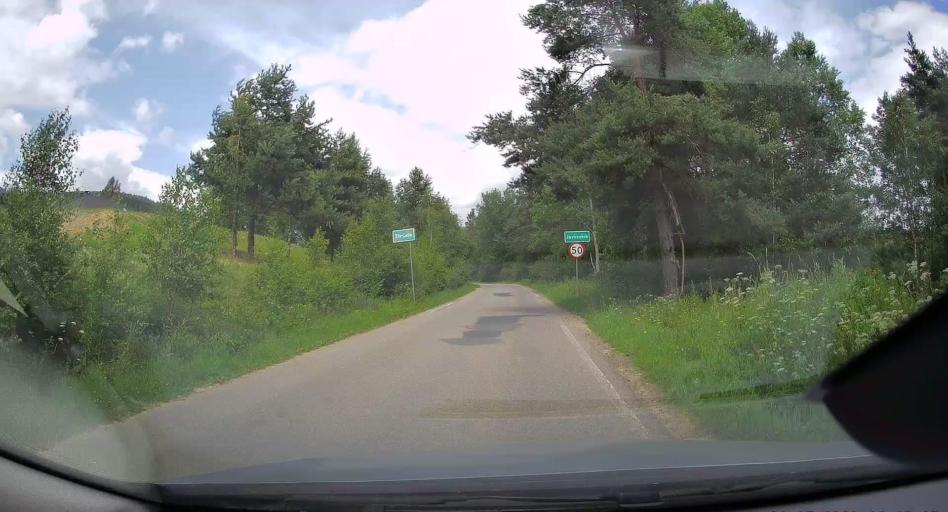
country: PL
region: Lesser Poland Voivodeship
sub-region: Powiat nowosadecki
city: Muszyna
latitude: 49.3860
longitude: 20.9017
